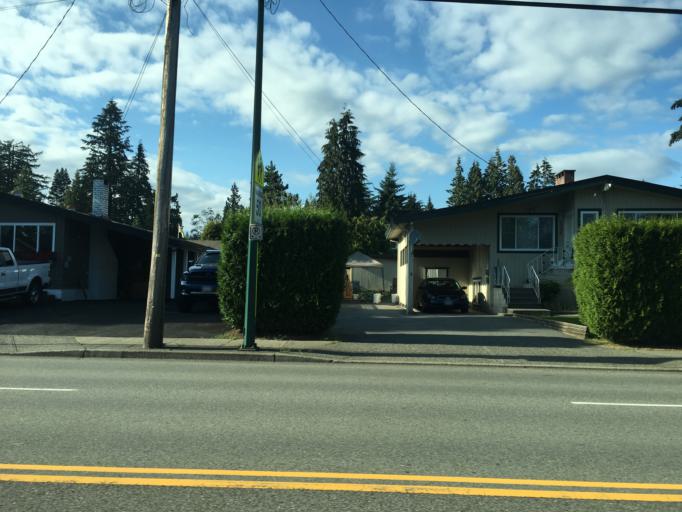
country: CA
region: British Columbia
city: Port Moody
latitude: 49.2490
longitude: -122.8319
